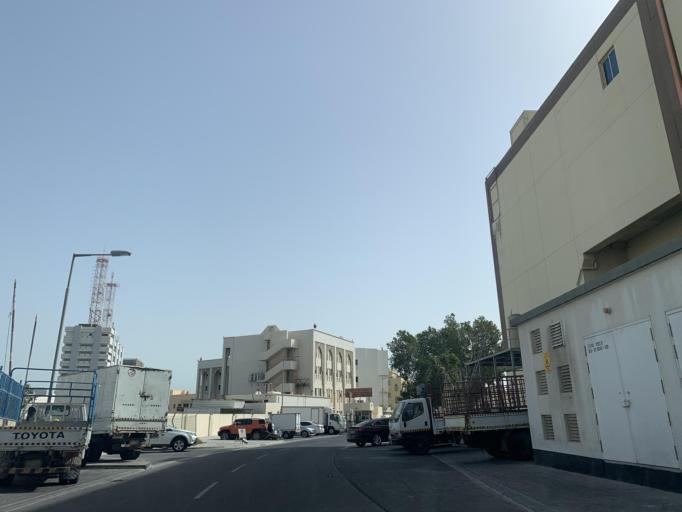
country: BH
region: Manama
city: Manama
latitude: 26.2197
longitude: 50.5687
